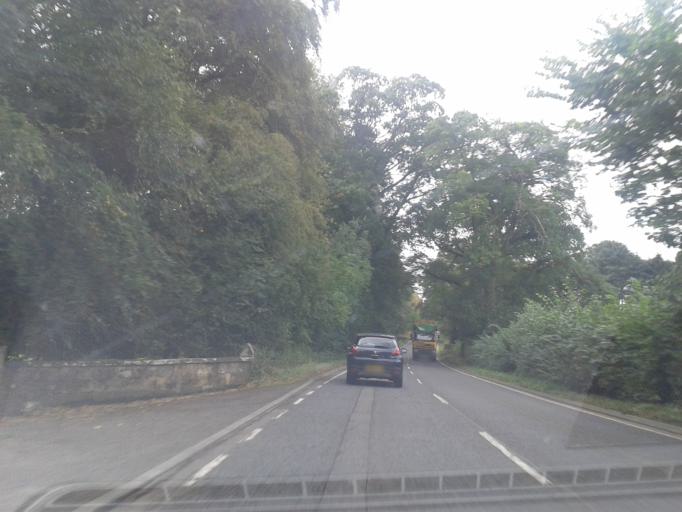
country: GB
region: Scotland
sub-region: Fife
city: Ladybank
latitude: 56.3028
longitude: -3.1049
